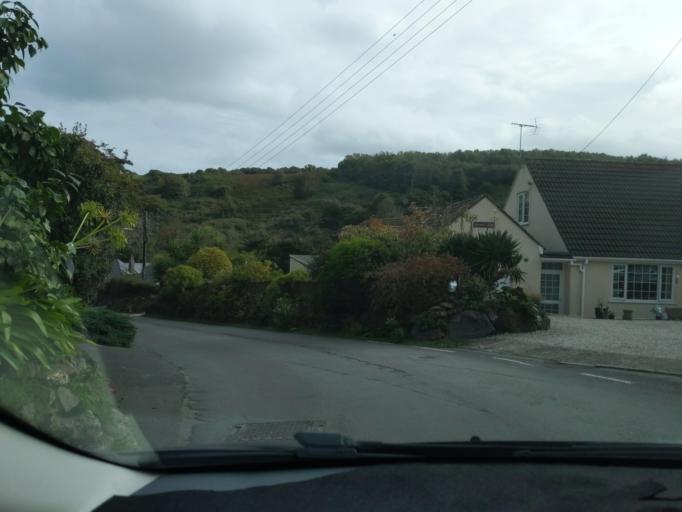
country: GB
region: England
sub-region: Cornwall
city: Mevagissey
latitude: 50.2396
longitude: -4.7957
